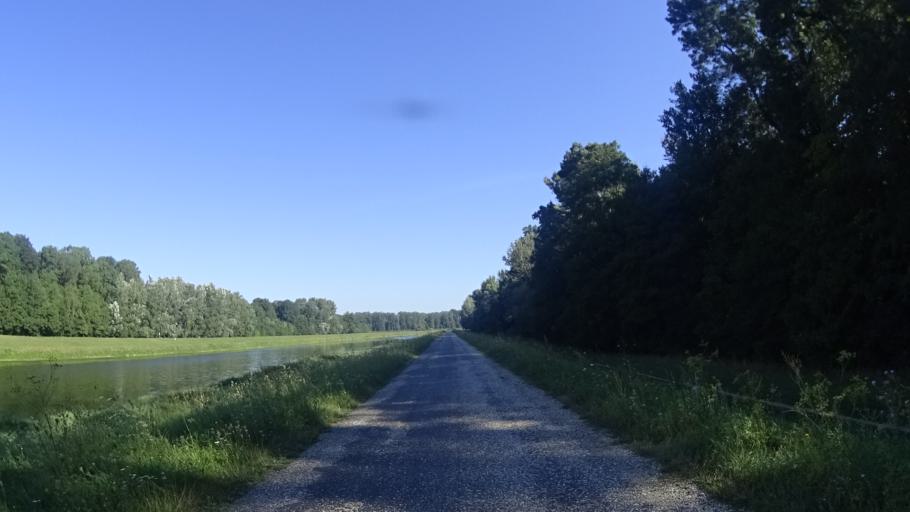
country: CZ
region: South Moravian
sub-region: Okres Breclav
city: Lanzhot
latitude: 48.7002
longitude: 16.9988
